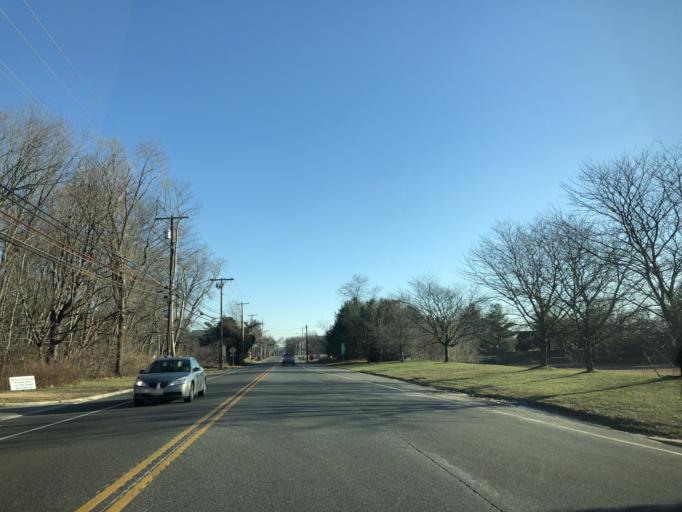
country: US
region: New Jersey
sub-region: Salem County
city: Carneys Point
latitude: 39.7034
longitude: -75.4411
